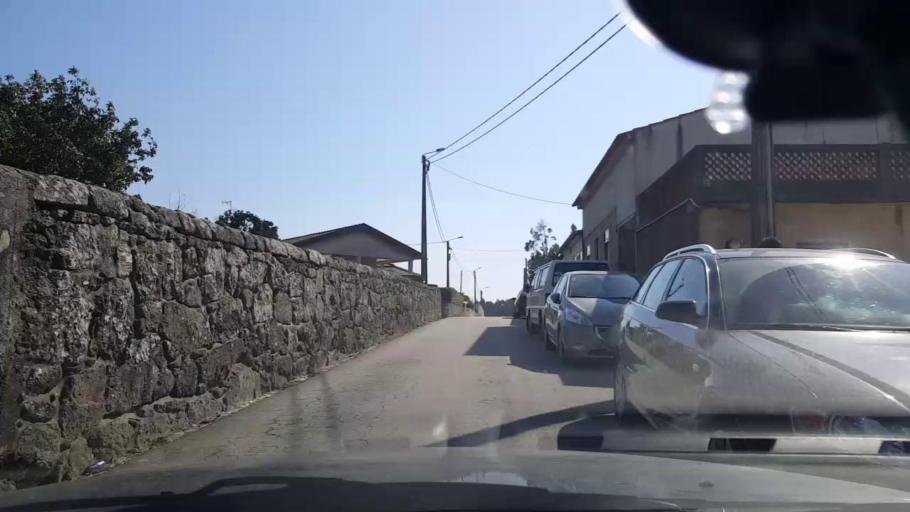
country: PT
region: Porto
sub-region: Vila do Conde
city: Vila do Conde
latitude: 41.3841
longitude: -8.7184
